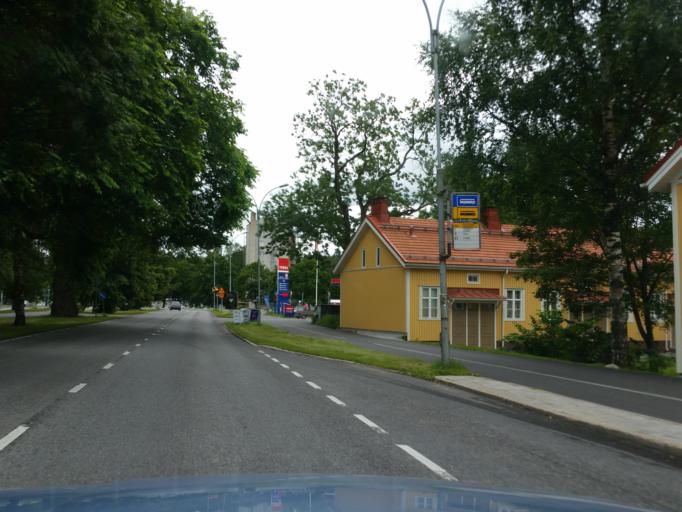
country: FI
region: Varsinais-Suomi
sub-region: Turku
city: Turku
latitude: 60.4384
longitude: 22.2912
